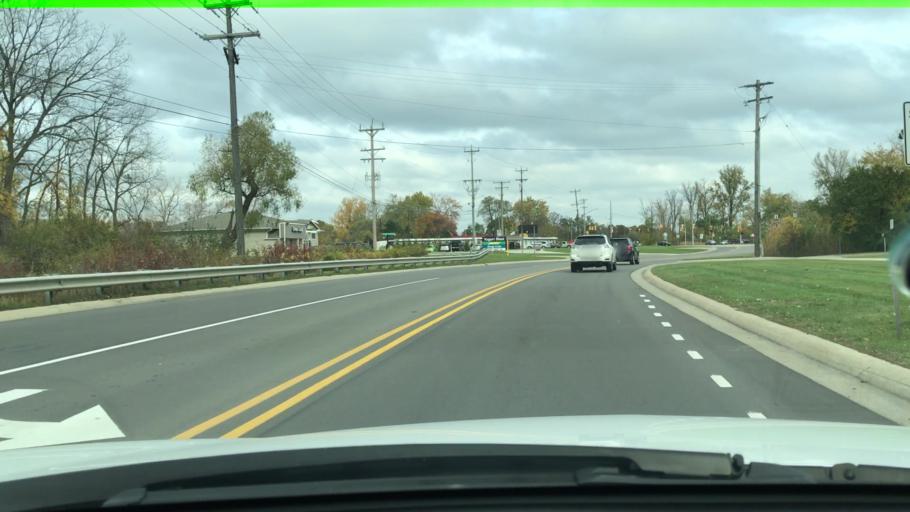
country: US
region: Michigan
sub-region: Oakland County
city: Waterford
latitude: 42.6582
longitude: -83.4434
